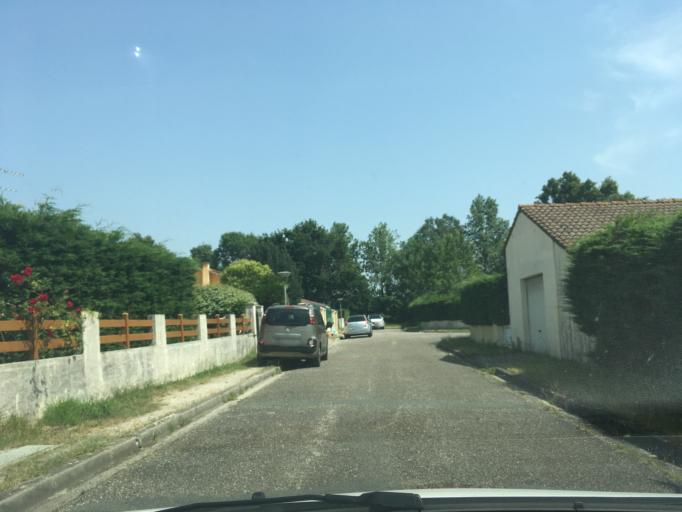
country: FR
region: Aquitaine
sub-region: Departement de la Gironde
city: Cantenac
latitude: 45.0248
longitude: -0.6352
